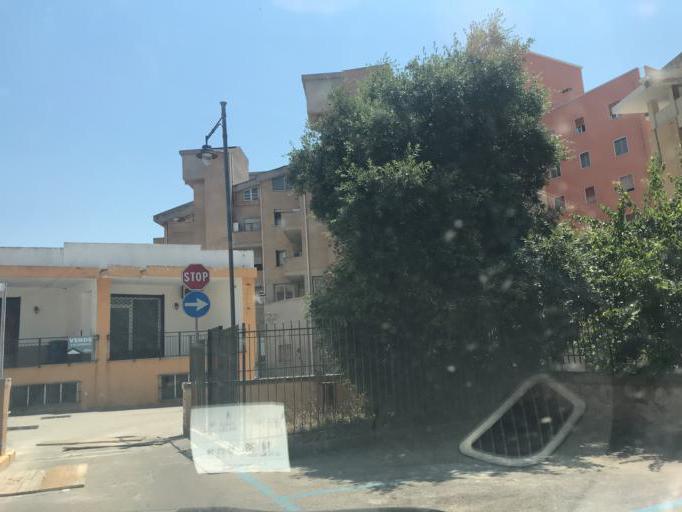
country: IT
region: Sardinia
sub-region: Provincia di Olbia-Tempio
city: Olbia
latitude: 40.9220
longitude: 9.4978
